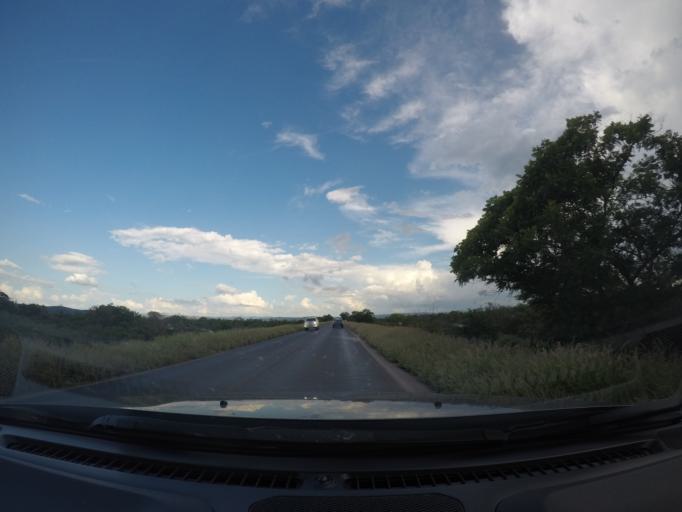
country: BR
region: Bahia
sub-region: Ibotirama
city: Ibotirama
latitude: -12.1551
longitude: -43.3061
